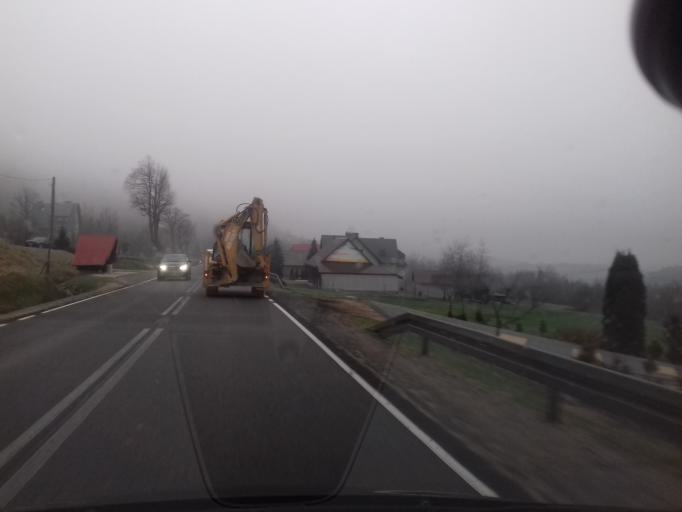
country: PL
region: Lesser Poland Voivodeship
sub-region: Powiat limanowski
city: Kasina Wielka
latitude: 49.7000
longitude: 20.1790
